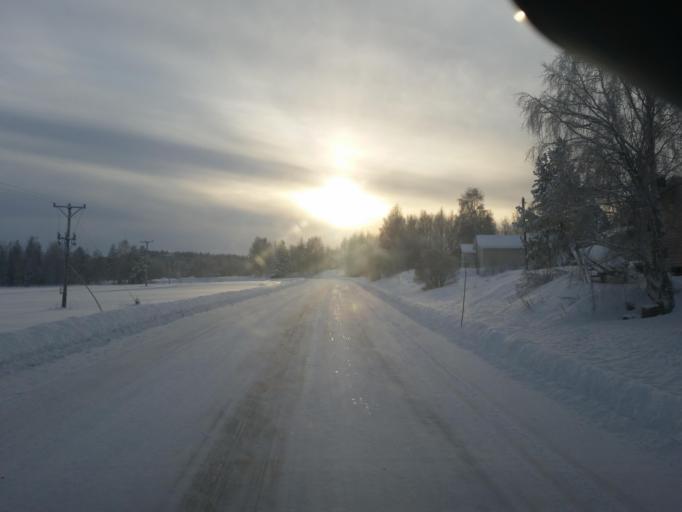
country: SE
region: Norrbotten
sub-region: Pitea Kommun
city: Norrfjarden
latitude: 65.5236
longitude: 21.4917
